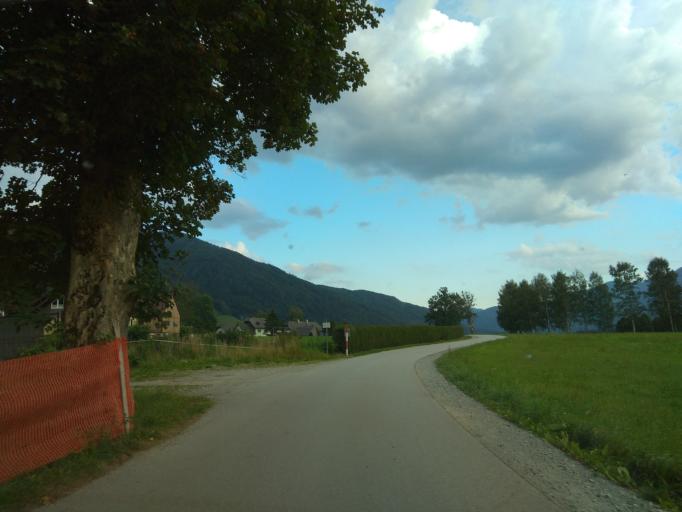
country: AT
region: Styria
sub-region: Politischer Bezirk Leoben
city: Vordernberg
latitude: 47.5359
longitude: 15.0691
